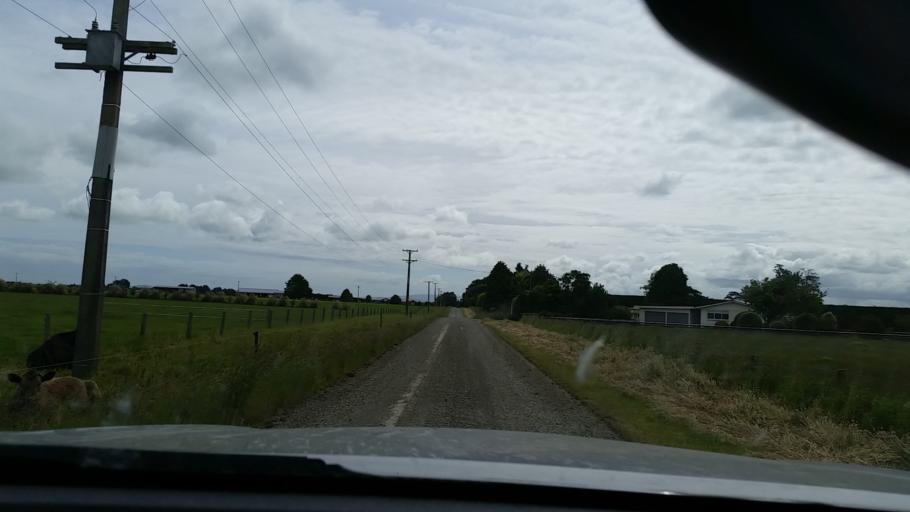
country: NZ
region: Southland
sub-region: Invercargill City
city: Invercargill
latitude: -46.2991
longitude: 168.2450
